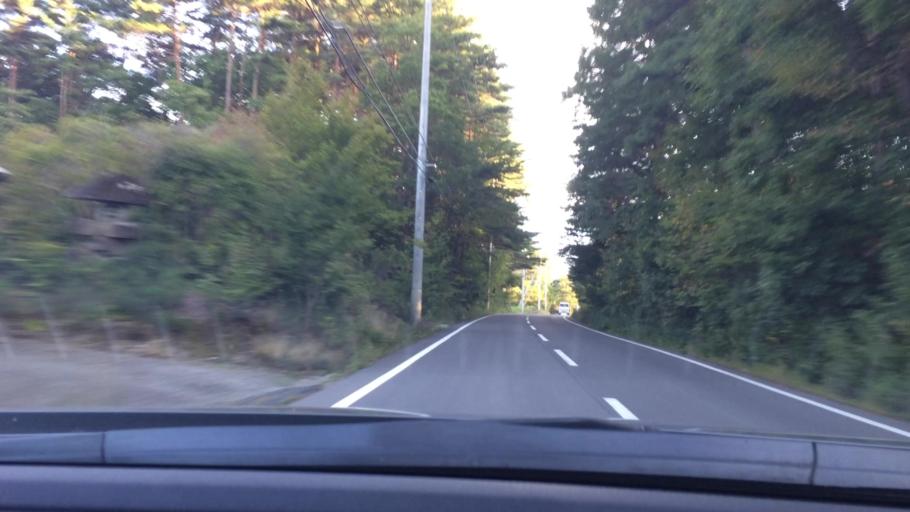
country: JP
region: Nagano
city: Komoro
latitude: 36.4931
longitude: 138.5115
